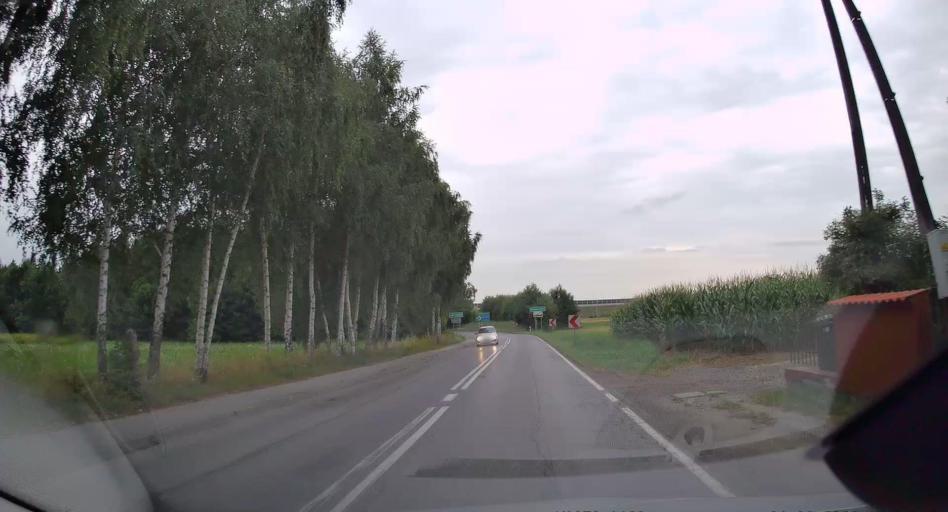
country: PL
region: Lesser Poland Voivodeship
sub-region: Powiat tarnowski
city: Wierzchoslawice
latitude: 50.0095
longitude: 20.8681
